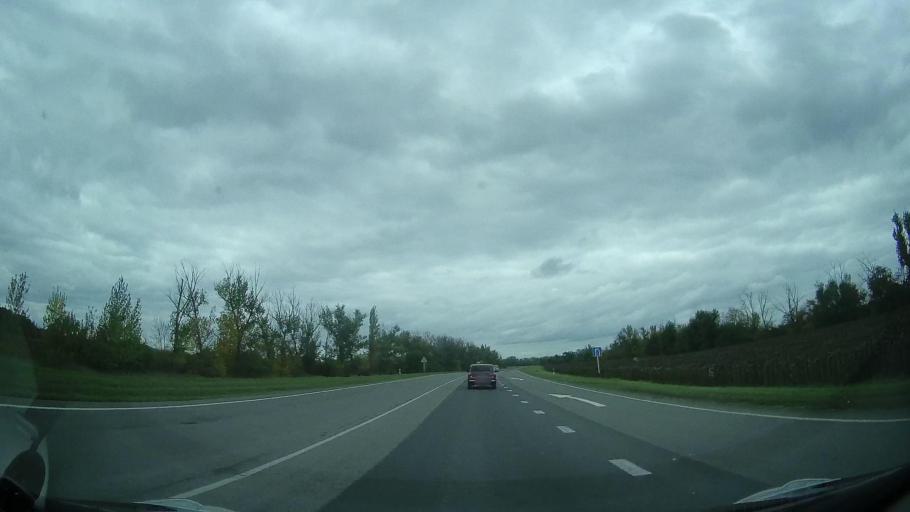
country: RU
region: Rostov
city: Yegorlykskaya
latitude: 46.5389
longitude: 40.7772
